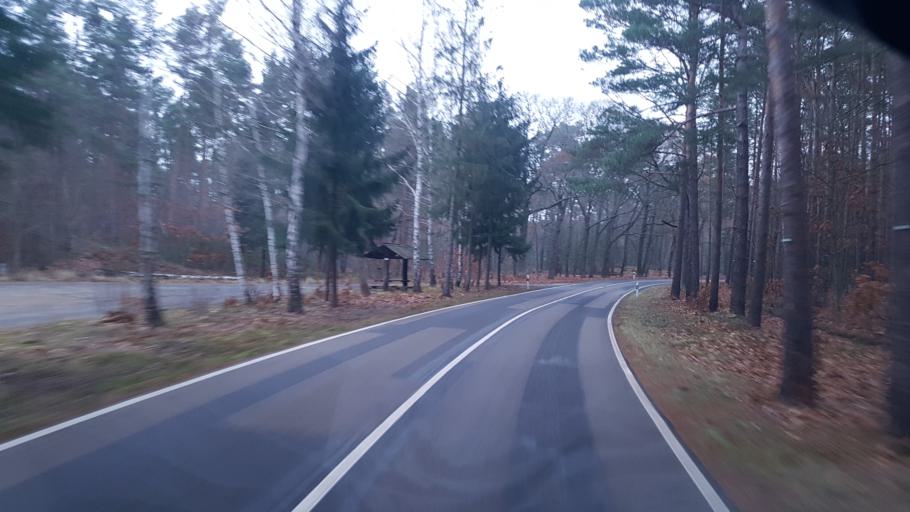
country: DE
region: Brandenburg
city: Drachhausen
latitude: 51.8704
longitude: 14.2727
